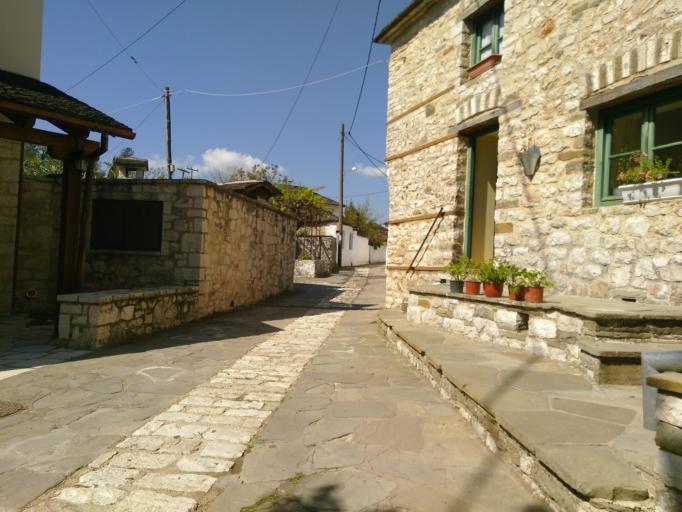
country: GR
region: Epirus
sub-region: Nomos Ioanninon
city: Ioannina
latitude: 39.6808
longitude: 20.8744
